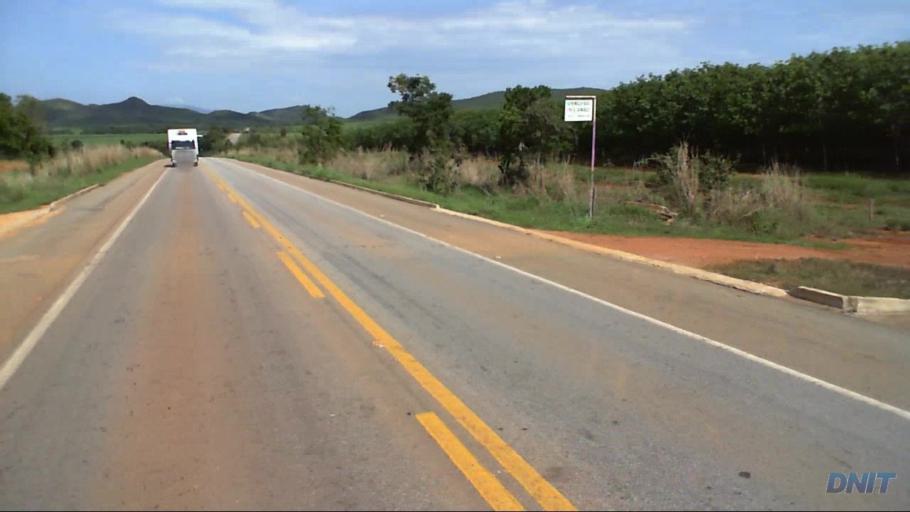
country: BR
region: Goias
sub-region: Barro Alto
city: Barro Alto
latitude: -15.1934
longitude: -48.7704
